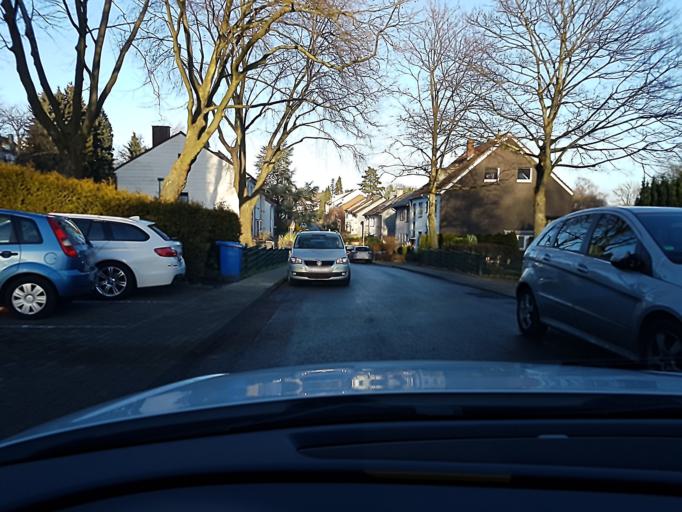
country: DE
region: North Rhine-Westphalia
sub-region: Regierungsbezirk Dusseldorf
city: Essen
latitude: 51.4328
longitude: 7.0451
